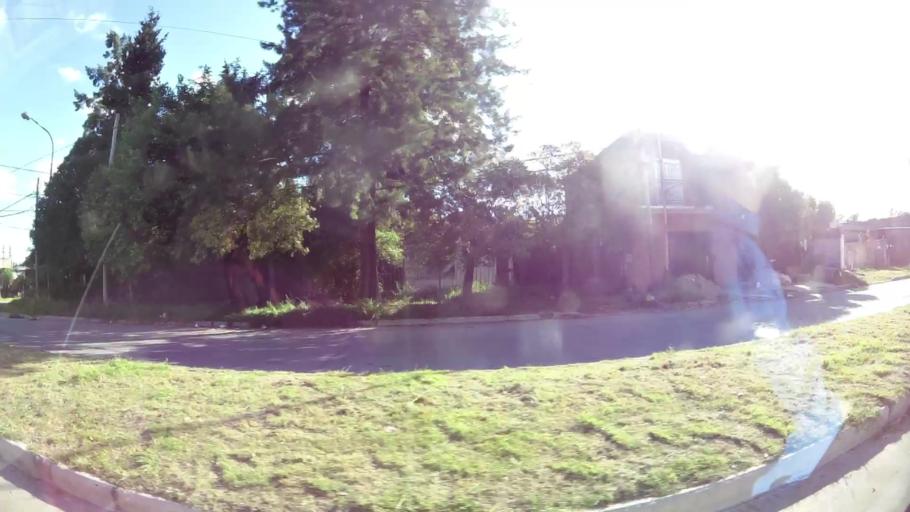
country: AR
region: Buenos Aires
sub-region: Partido de Moron
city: Moron
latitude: -34.6852
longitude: -58.6041
